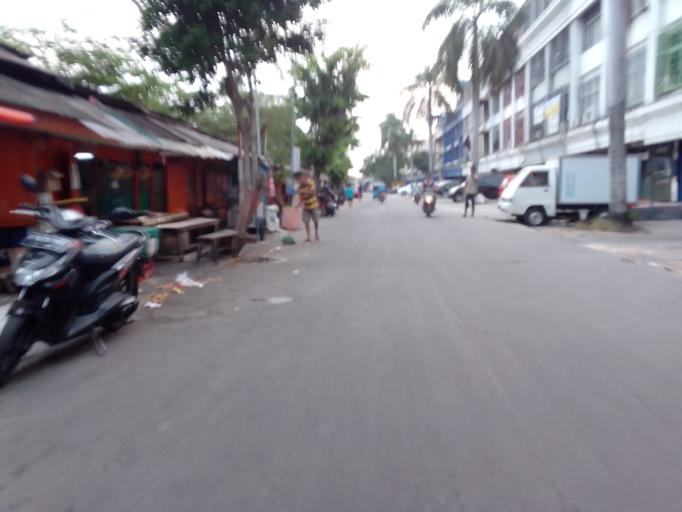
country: ID
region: Jakarta Raya
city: Jakarta
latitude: -6.1640
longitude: 106.8076
